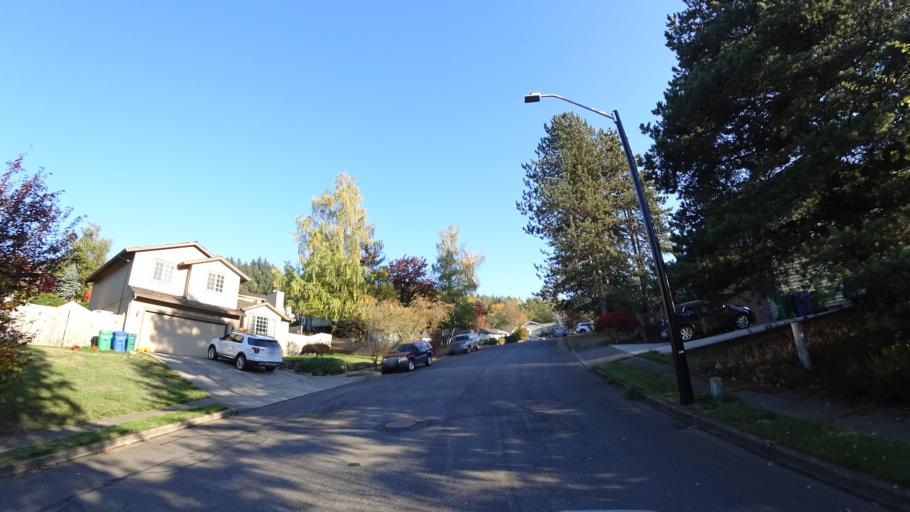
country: US
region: Oregon
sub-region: Multnomah County
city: Gresham
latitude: 45.4870
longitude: -122.4473
